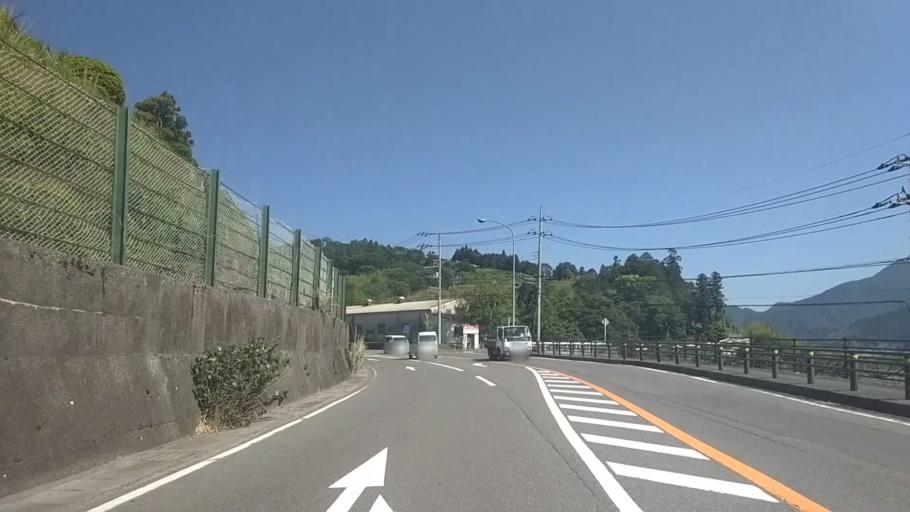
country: JP
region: Shizuoka
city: Fujinomiya
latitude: 35.2616
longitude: 138.4694
